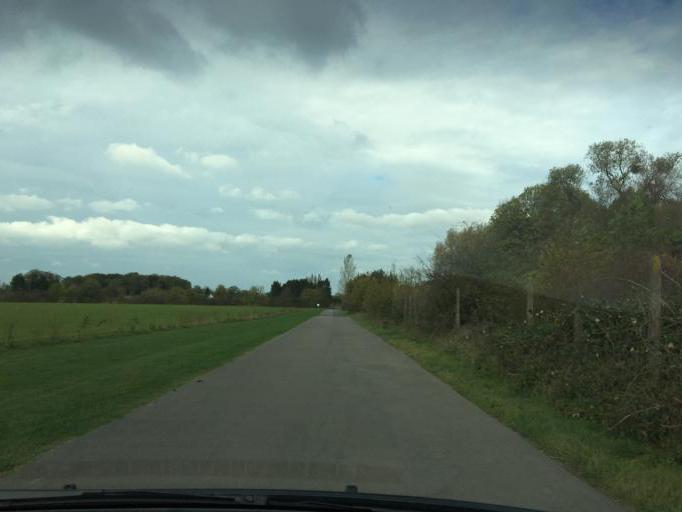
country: DE
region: North Rhine-Westphalia
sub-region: Regierungsbezirk Koln
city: Dueren
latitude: 50.7828
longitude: 6.4786
